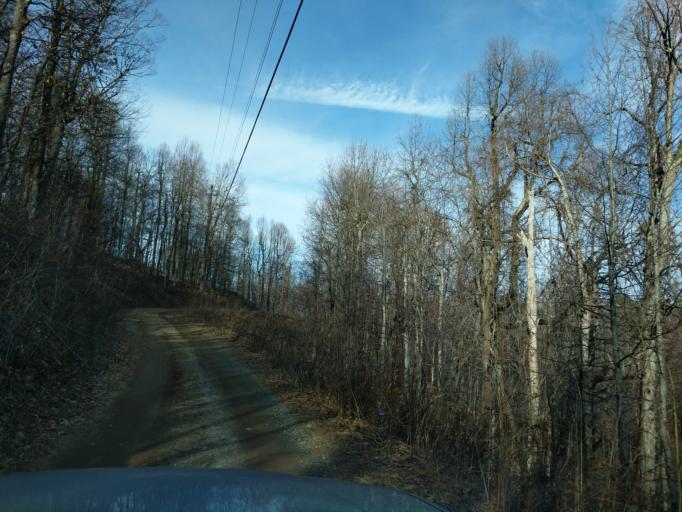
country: US
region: North Carolina
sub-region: Polk County
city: Columbus
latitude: 35.2725
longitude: -82.2323
